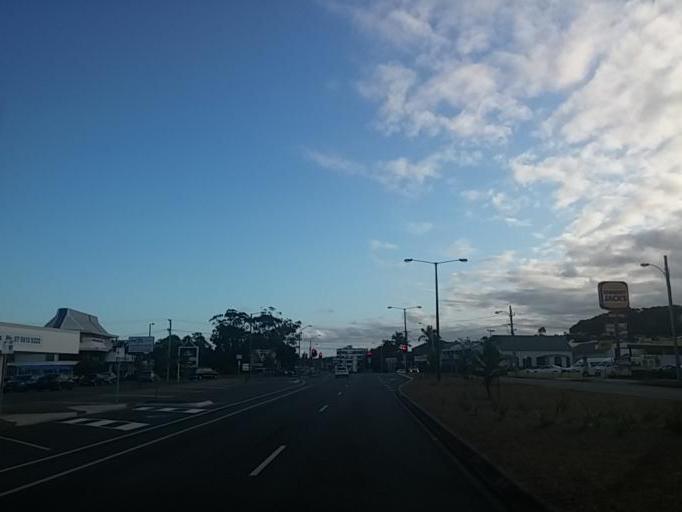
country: AU
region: New South Wales
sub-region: Tweed
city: Tweed Heads West
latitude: -28.1749
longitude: 153.5422
